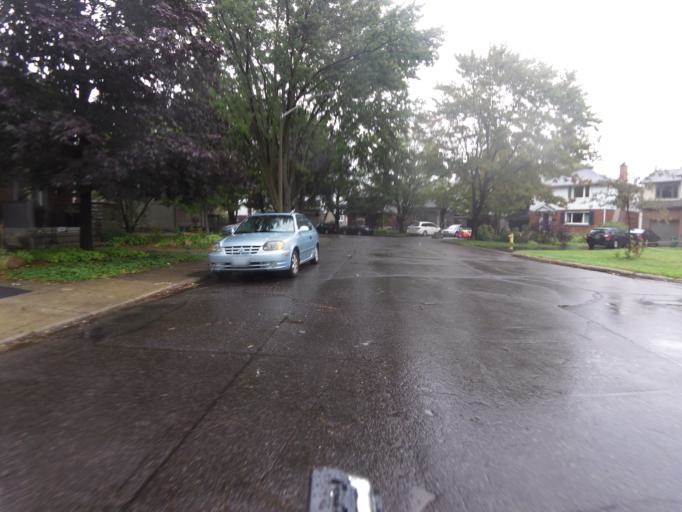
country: CA
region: Ontario
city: Ottawa
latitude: 45.4006
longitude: -75.6727
